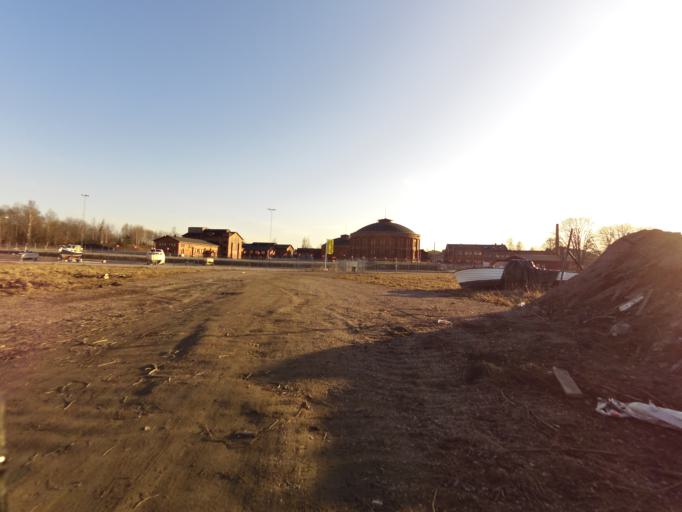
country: SE
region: Gaevleborg
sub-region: Gavle Kommun
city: Gavle
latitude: 60.6797
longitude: 17.1786
